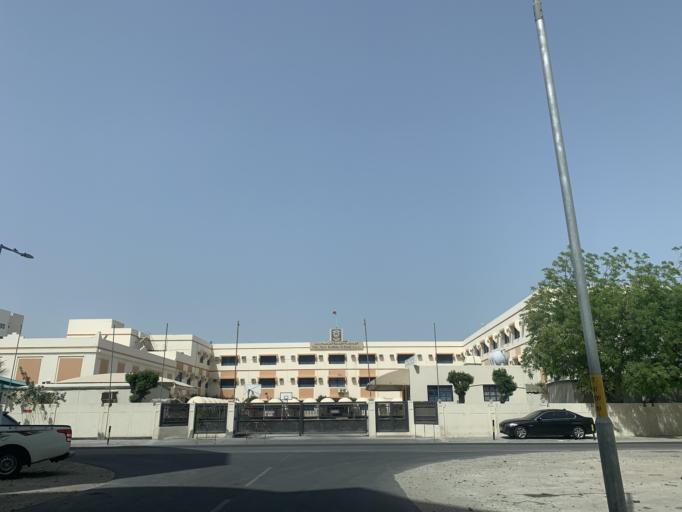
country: BH
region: Northern
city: Madinat `Isa
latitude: 26.1548
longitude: 50.5656
